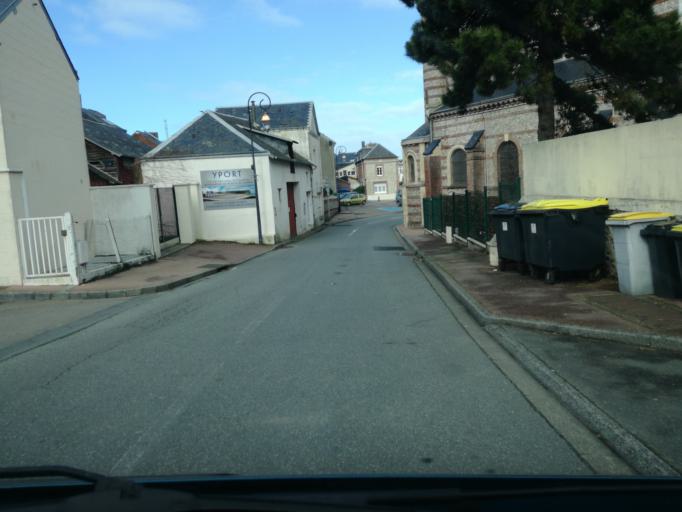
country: FR
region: Haute-Normandie
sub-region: Departement de la Seine-Maritime
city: Yport
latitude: 49.7373
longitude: 0.3141
